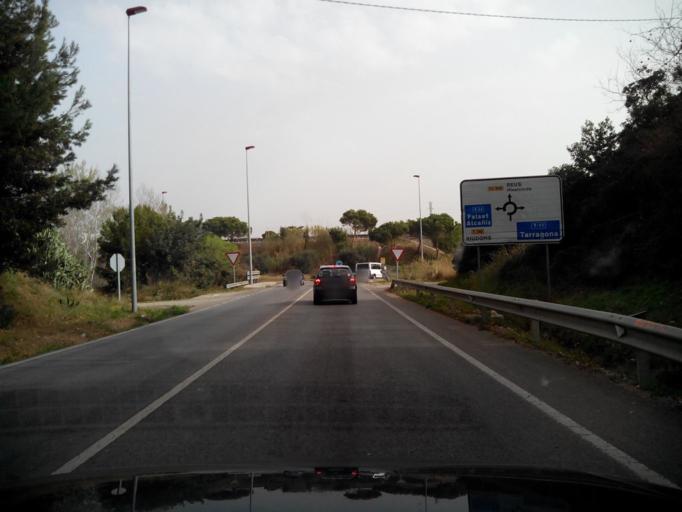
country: ES
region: Catalonia
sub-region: Provincia de Tarragona
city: Reus
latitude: 41.1386
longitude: 1.0976
